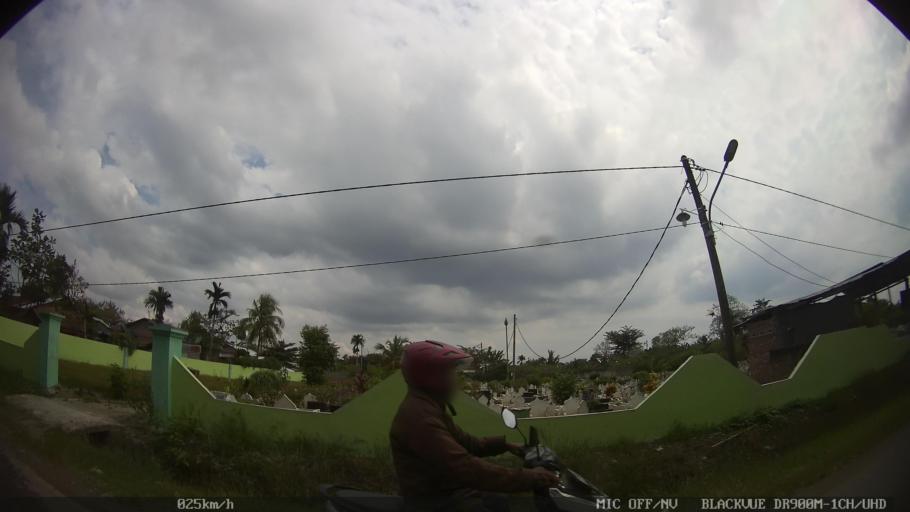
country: ID
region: North Sumatra
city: Sunggal
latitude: 3.6357
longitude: 98.6009
